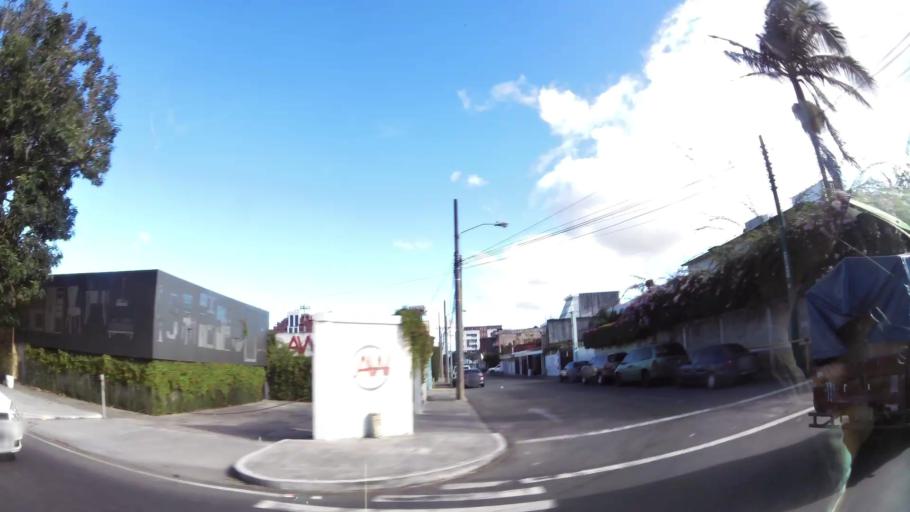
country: GT
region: Guatemala
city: Santa Catarina Pinula
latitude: 14.5893
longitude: -90.5082
